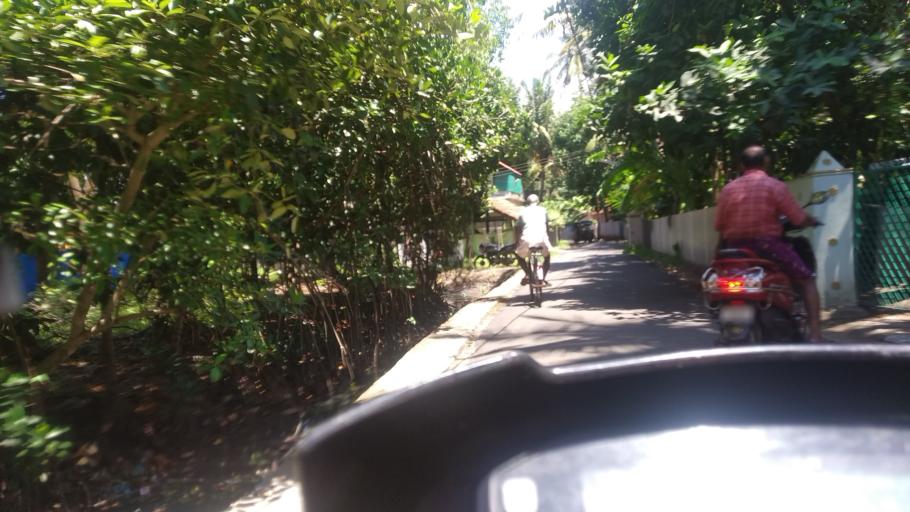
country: IN
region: Kerala
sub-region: Ernakulam
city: Elur
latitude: 10.0611
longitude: 76.2195
